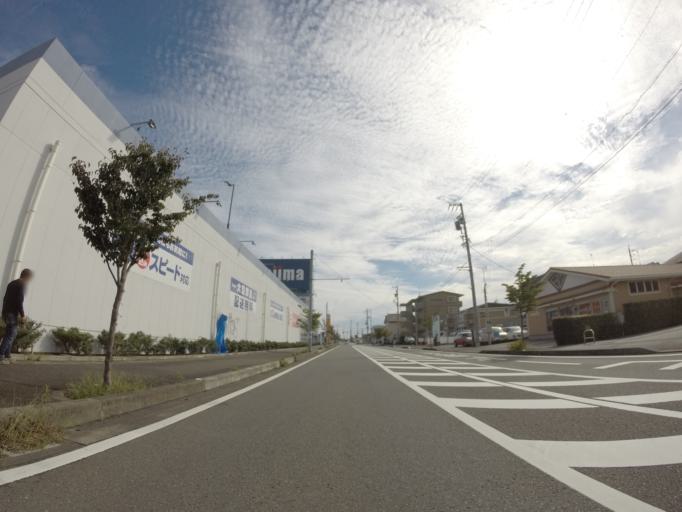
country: JP
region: Shizuoka
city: Fujieda
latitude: 34.8821
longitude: 138.2711
